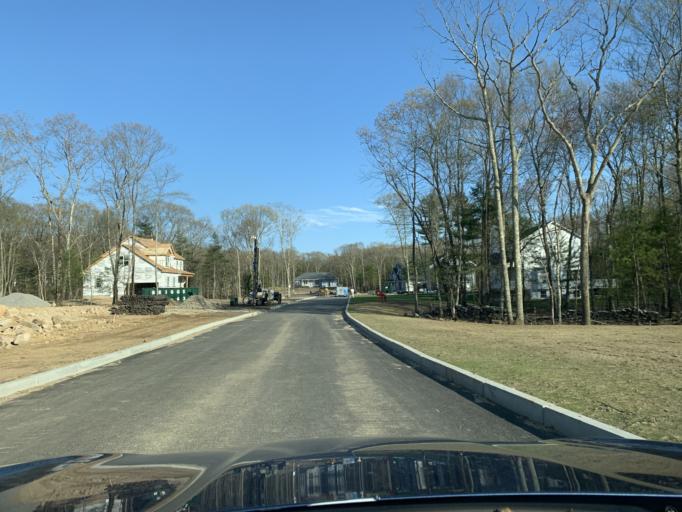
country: US
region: Rhode Island
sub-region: Washington County
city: Exeter
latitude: 41.6128
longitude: -71.5300
